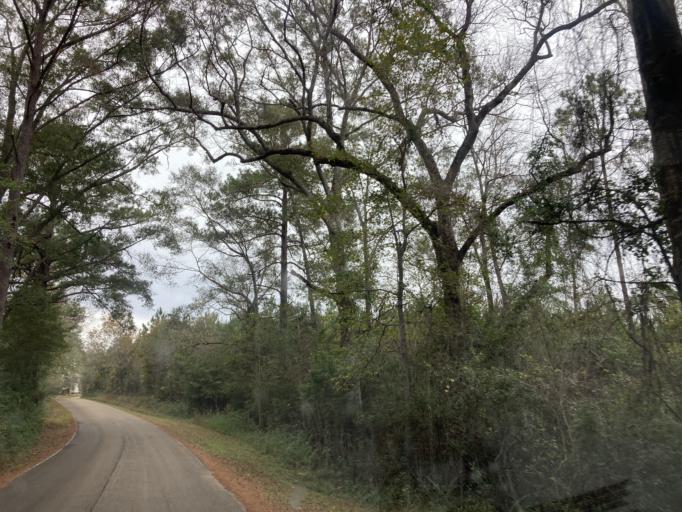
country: US
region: Mississippi
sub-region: Lamar County
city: Lumberton
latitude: 31.0361
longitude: -89.4548
